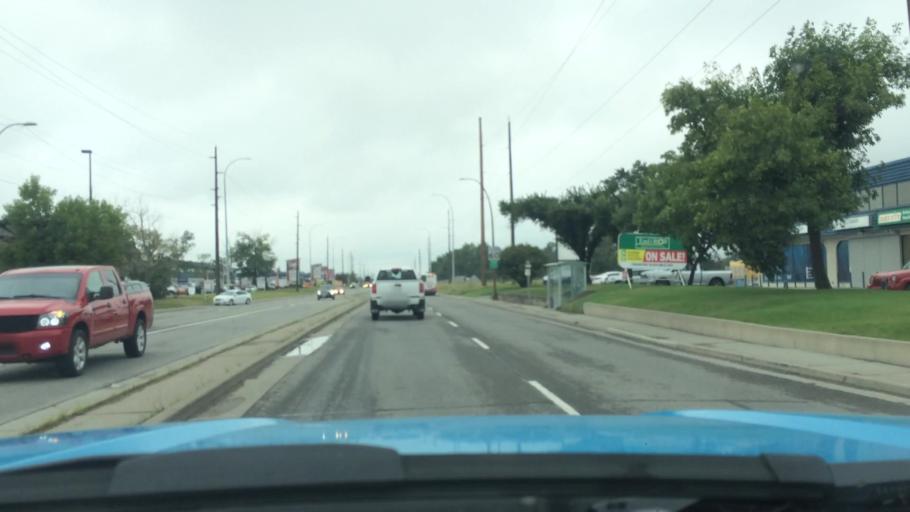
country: CA
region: Alberta
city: Calgary
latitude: 51.0815
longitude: -114.0121
